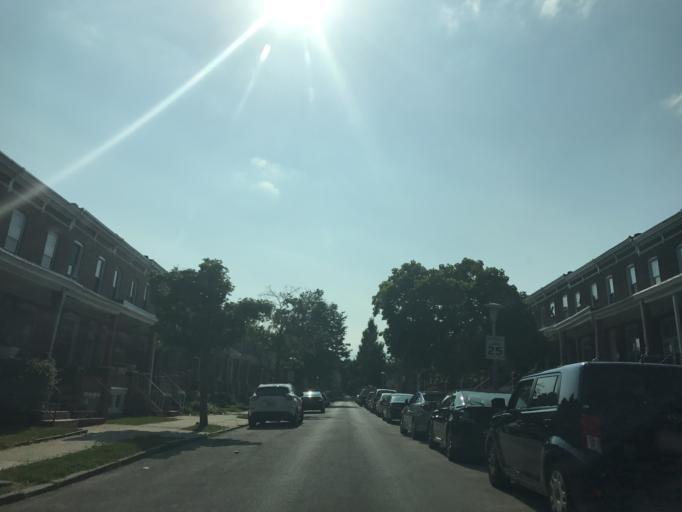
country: US
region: Maryland
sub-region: City of Baltimore
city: Baltimore
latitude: 39.3322
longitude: -76.6061
